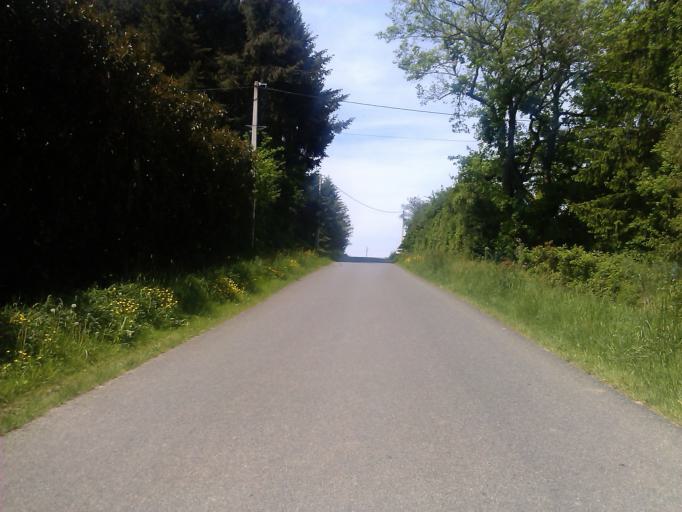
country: FR
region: Centre
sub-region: Departement du Cher
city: Le Chatelet
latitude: 46.5821
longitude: 2.3818
